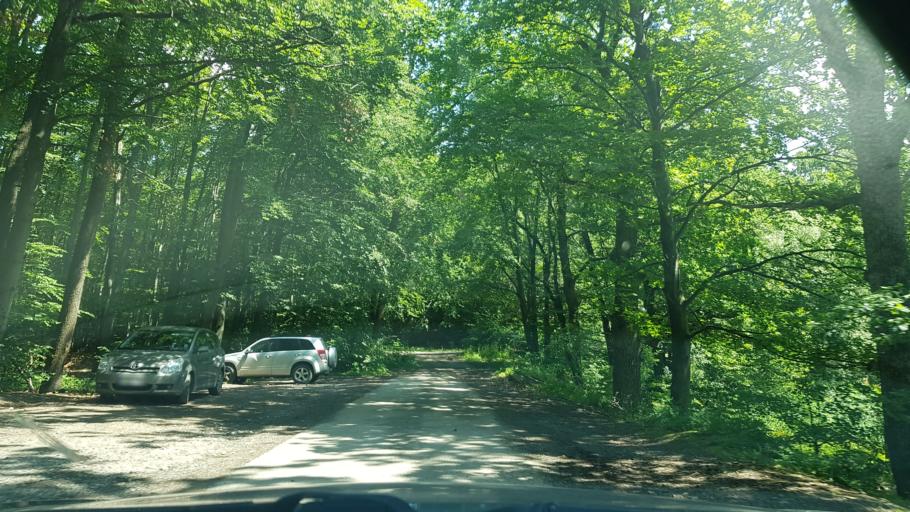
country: SK
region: Kosicky
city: Secovce
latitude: 48.5708
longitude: 21.4941
